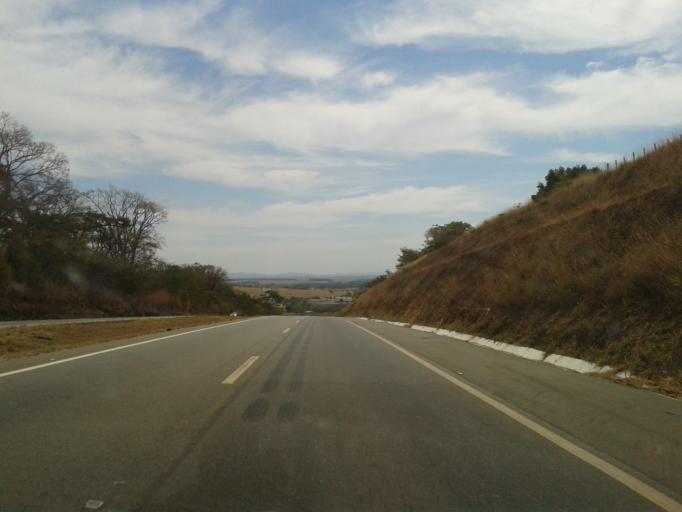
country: BR
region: Goias
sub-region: Itaberai
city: Itaberai
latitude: -16.1442
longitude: -49.6366
